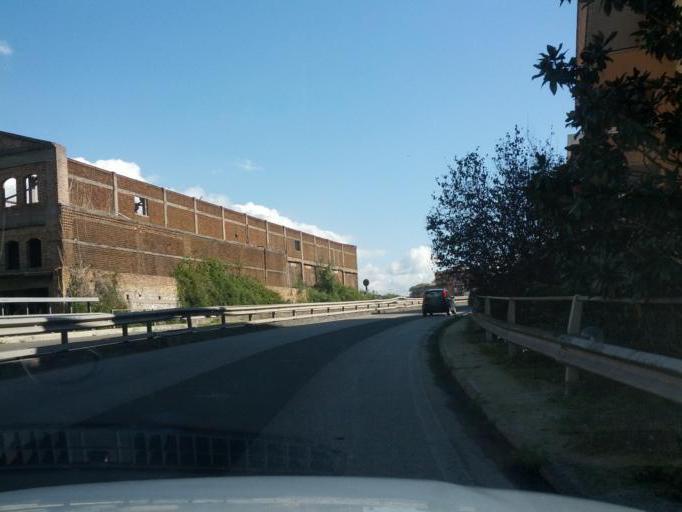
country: IT
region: Latium
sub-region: Provincia di Latina
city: Formia
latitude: 41.2646
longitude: 13.6219
